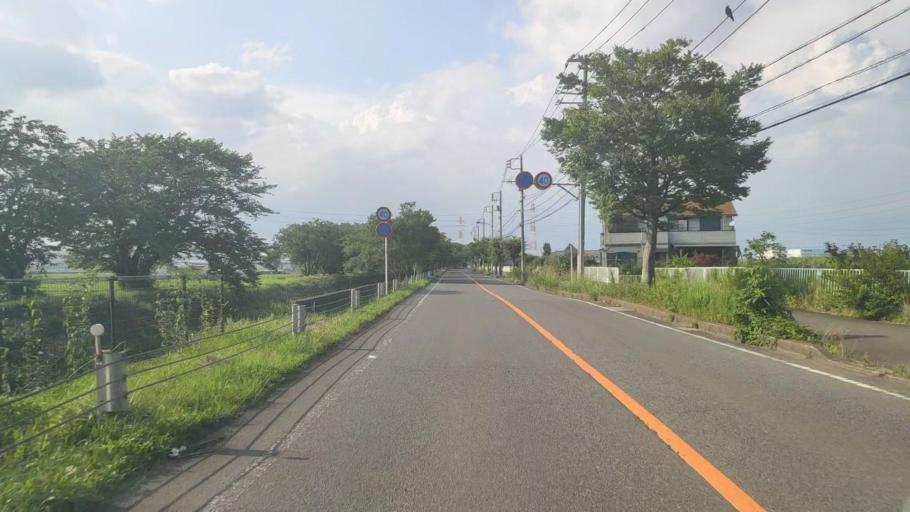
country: JP
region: Kanagawa
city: Isehara
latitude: 35.3924
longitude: 139.3379
